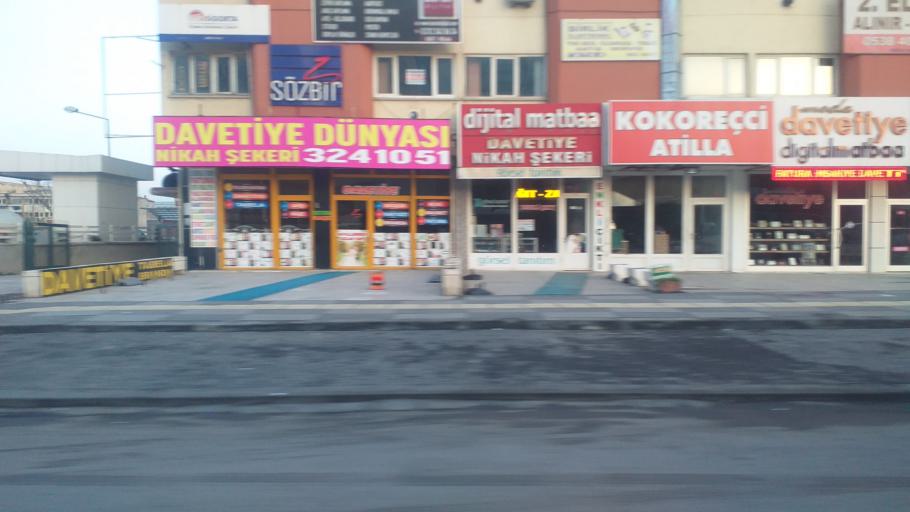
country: TR
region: Ankara
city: Ankara
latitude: 39.9459
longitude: 32.8480
